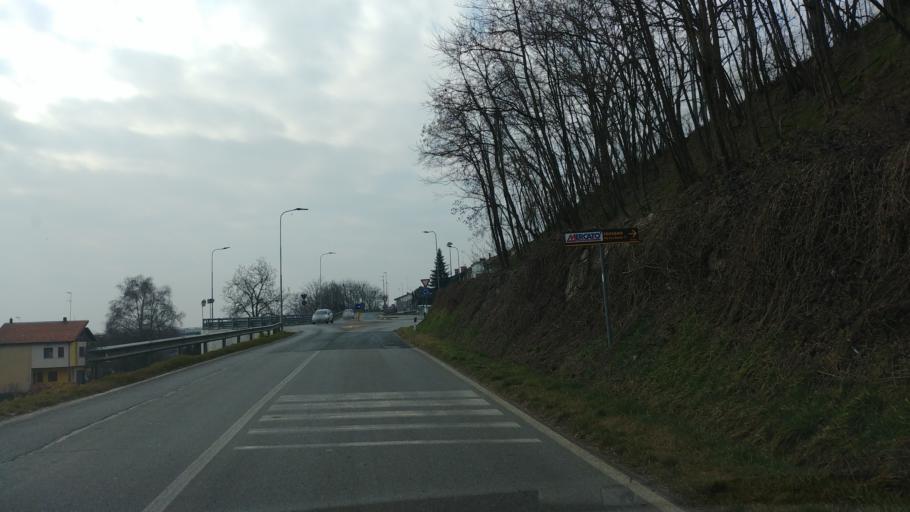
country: IT
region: Piedmont
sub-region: Provincia di Cuneo
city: Fossano
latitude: 44.5435
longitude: 7.7252
